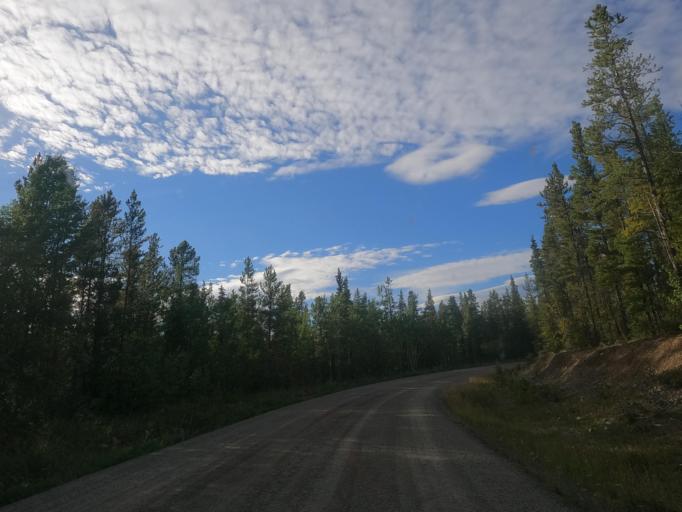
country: CA
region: Yukon
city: Whitehorse
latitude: 60.7553
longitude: -135.0370
